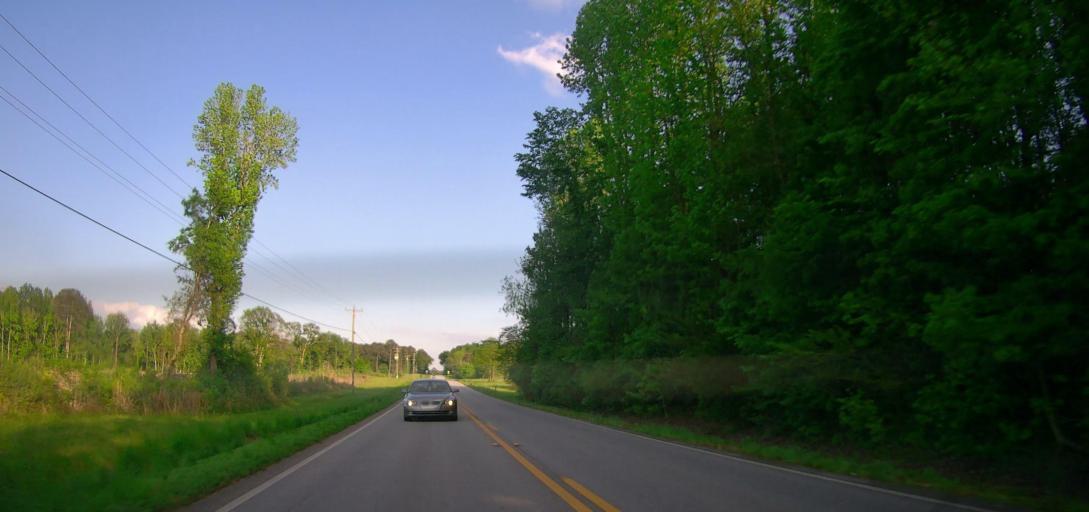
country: US
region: Georgia
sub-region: Jasper County
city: Monticello
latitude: 33.3783
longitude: -83.5456
